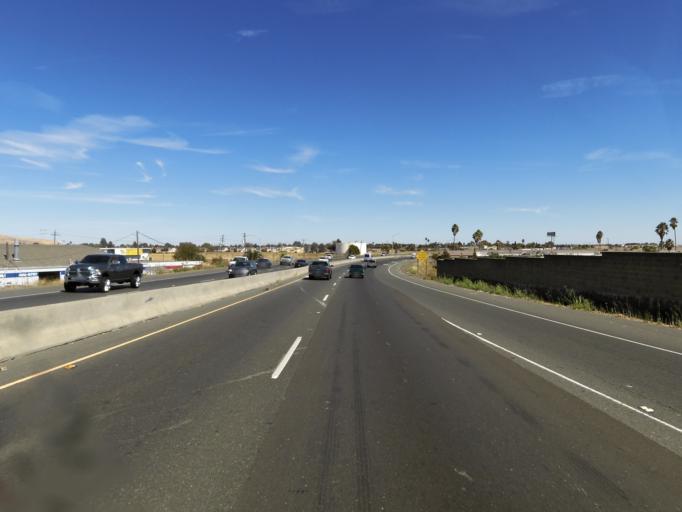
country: US
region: California
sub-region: Solano County
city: Fairfield
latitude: 38.2445
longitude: -122.0381
